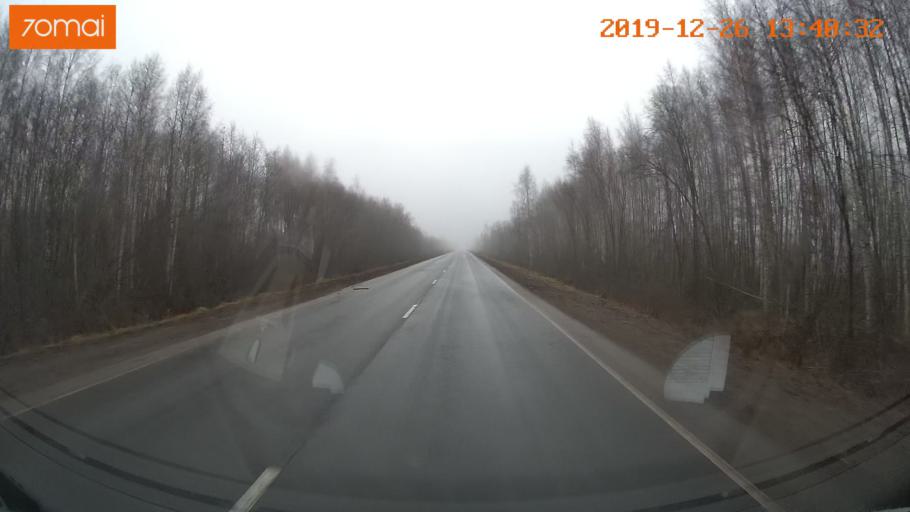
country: RU
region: Vologda
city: Sheksna
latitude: 58.7415
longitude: 38.4314
